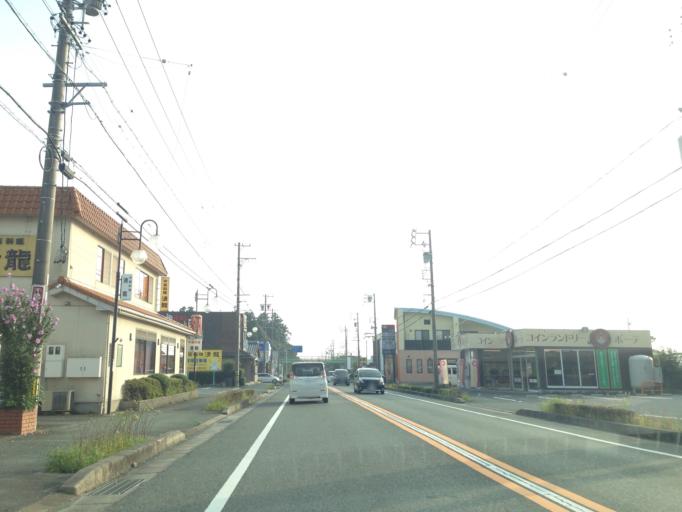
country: JP
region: Aichi
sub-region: Tokai-shi
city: Toyokawa
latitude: 34.8511
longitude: 137.4197
